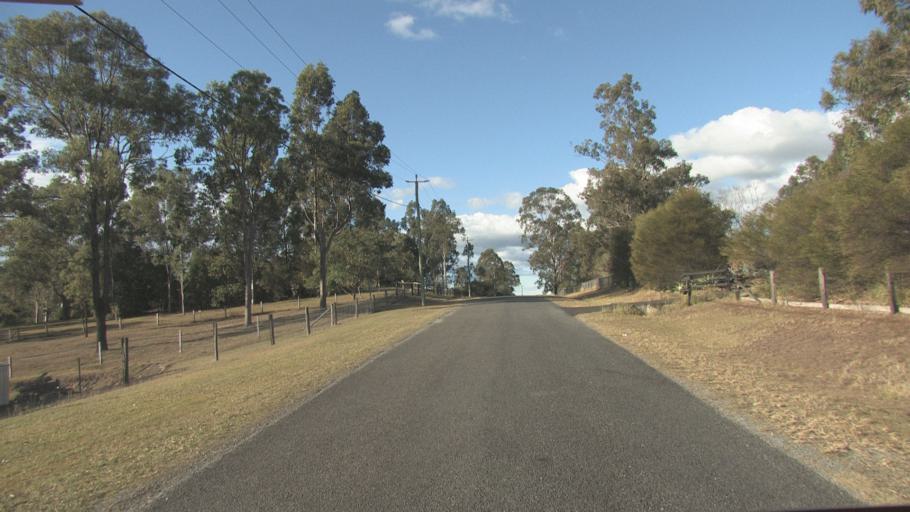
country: AU
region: Queensland
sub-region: Logan
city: Cedar Vale
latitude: -27.9320
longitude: 153.0619
